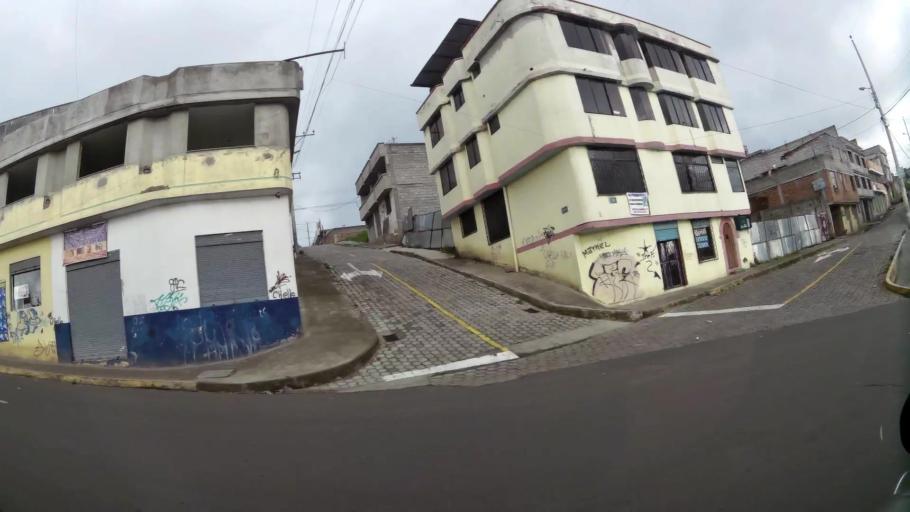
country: EC
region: Pichincha
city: Sangolqui
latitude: -0.3065
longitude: -78.5231
